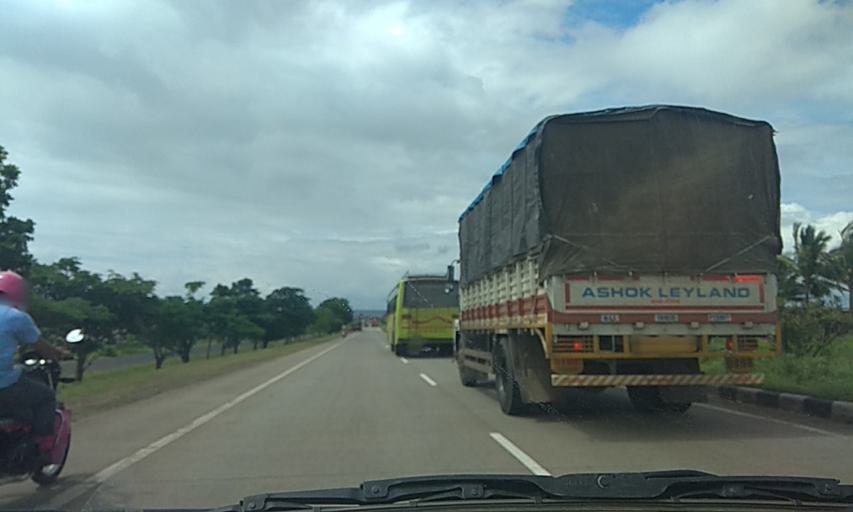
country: IN
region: Maharashtra
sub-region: Kolhapur
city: Kagal
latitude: 16.5114
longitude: 74.3295
